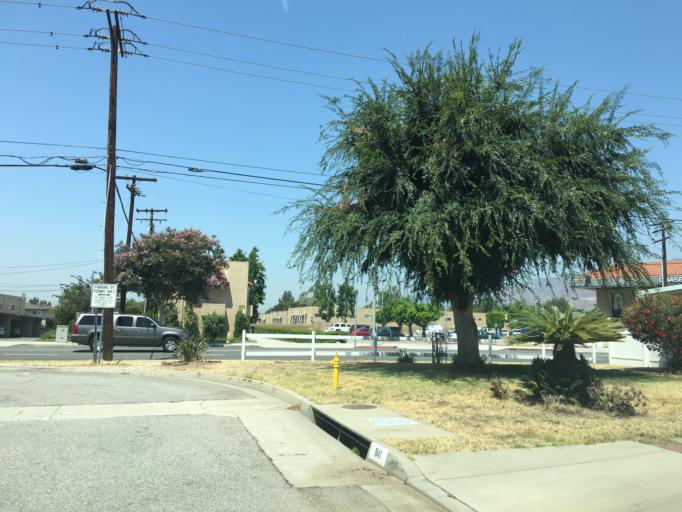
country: US
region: California
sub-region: Los Angeles County
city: Citrus
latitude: 34.1277
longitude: -117.8810
